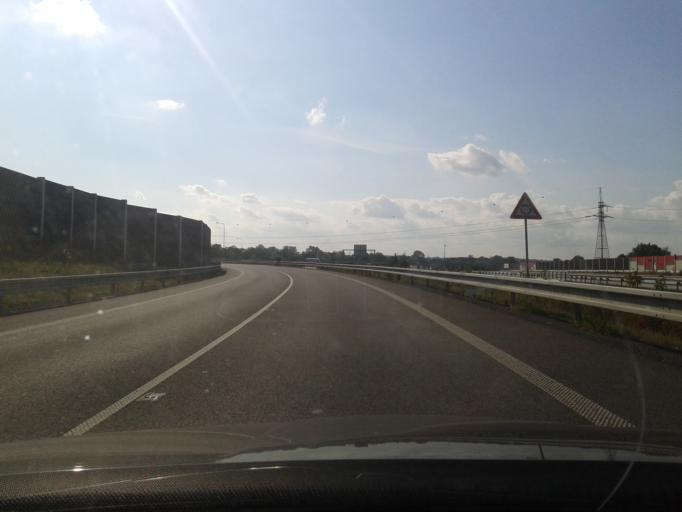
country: CZ
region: Moravskoslezsky
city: Stary Bohumin
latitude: 49.9117
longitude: 18.3381
